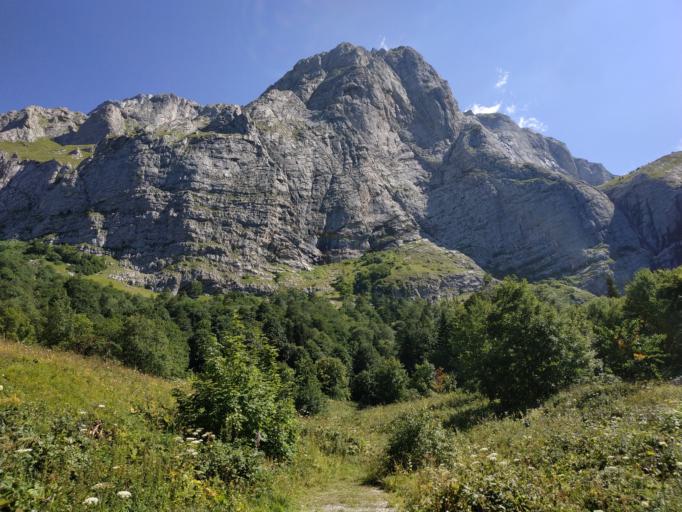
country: RU
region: Krasnodarskiy
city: Dagomys
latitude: 43.9786
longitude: 39.8743
